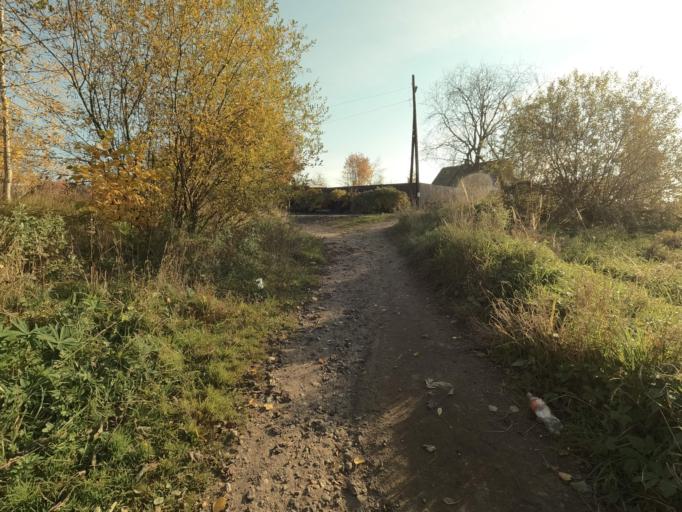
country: RU
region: Leningrad
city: Mga
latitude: 59.7529
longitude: 31.0616
